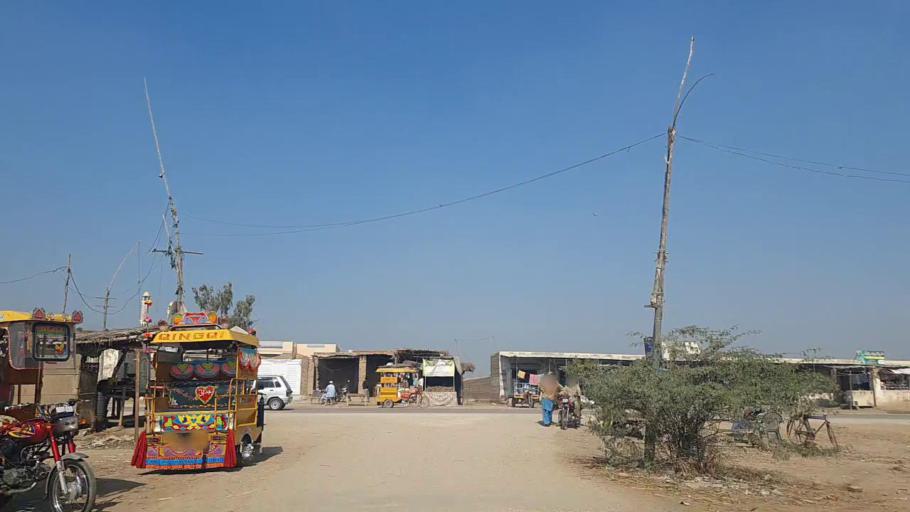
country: PK
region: Sindh
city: Nawabshah
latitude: 26.2548
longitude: 68.3411
